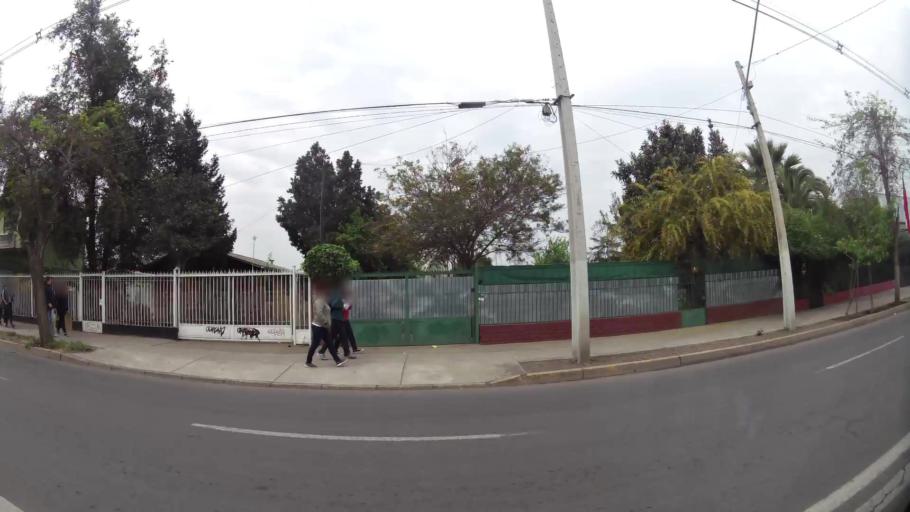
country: CL
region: Santiago Metropolitan
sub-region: Provincia de Chacabuco
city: Chicureo Abajo
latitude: -33.2086
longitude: -70.6791
